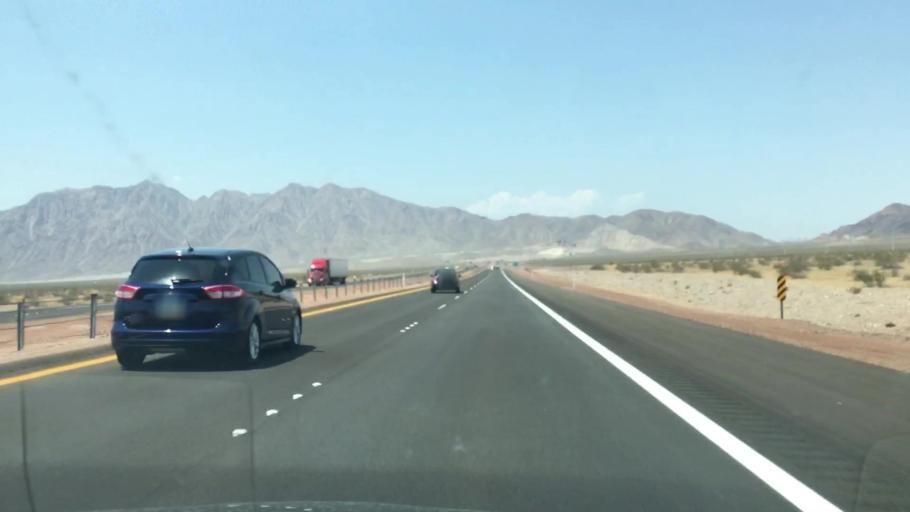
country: US
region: Nevada
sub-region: Clark County
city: Boulder City
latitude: 35.9388
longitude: -114.8725
